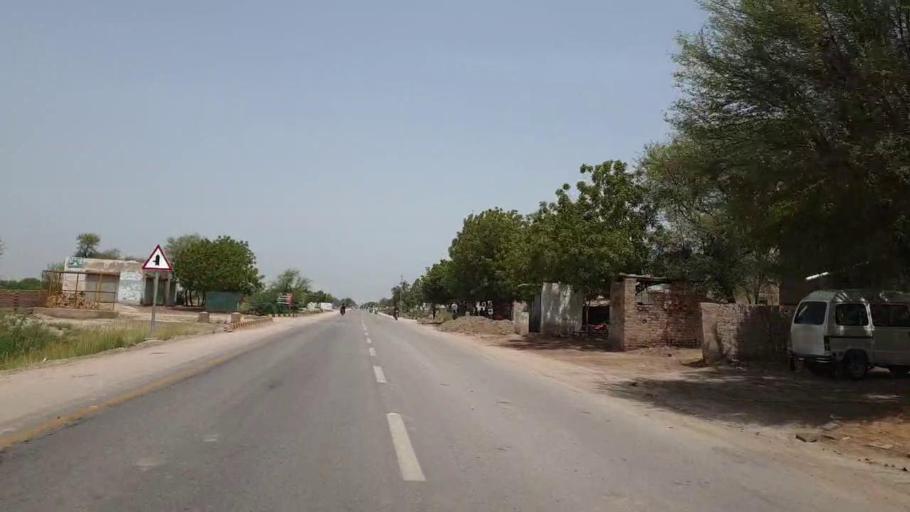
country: PK
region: Sindh
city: Shahpur Chakar
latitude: 26.1675
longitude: 68.6229
